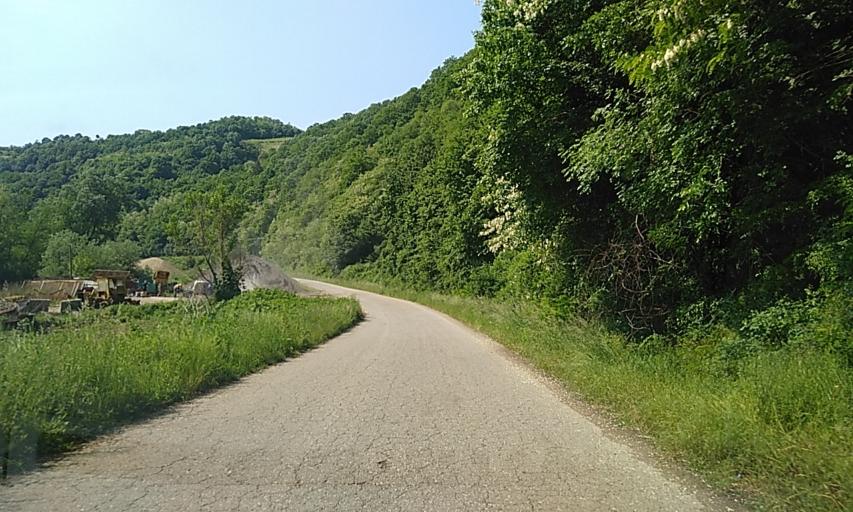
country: RS
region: Central Serbia
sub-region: Pcinjski Okrug
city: Vladicin Han
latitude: 42.7388
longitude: 22.0563
